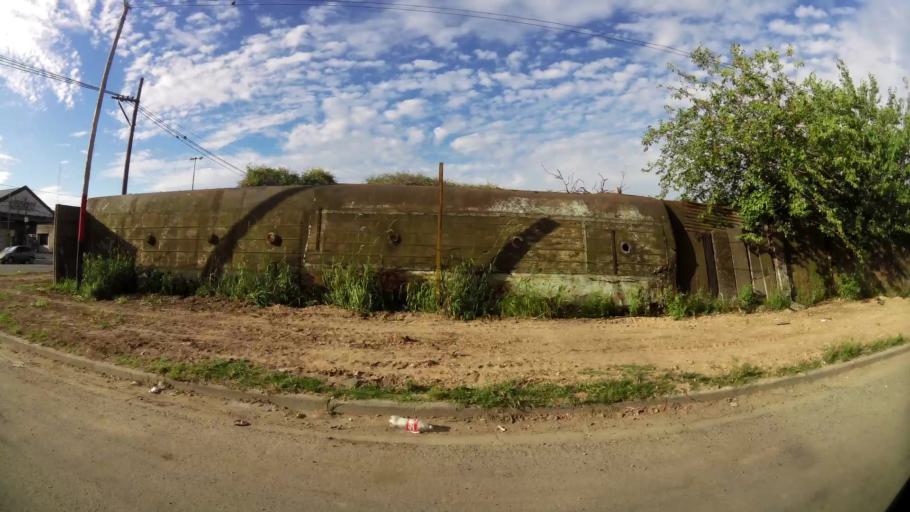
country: AR
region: Santa Fe
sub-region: Departamento de Rosario
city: Rosario
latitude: -32.9833
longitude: -60.6710
